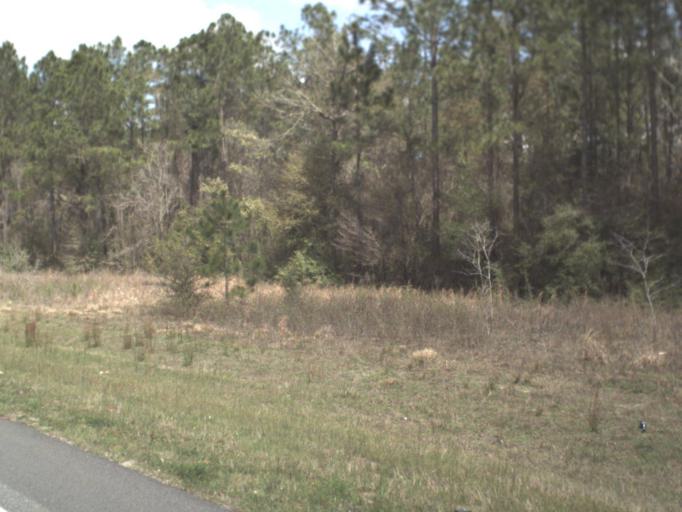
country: US
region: Florida
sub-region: Wakulla County
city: Crawfordville
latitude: 30.2521
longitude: -84.3623
